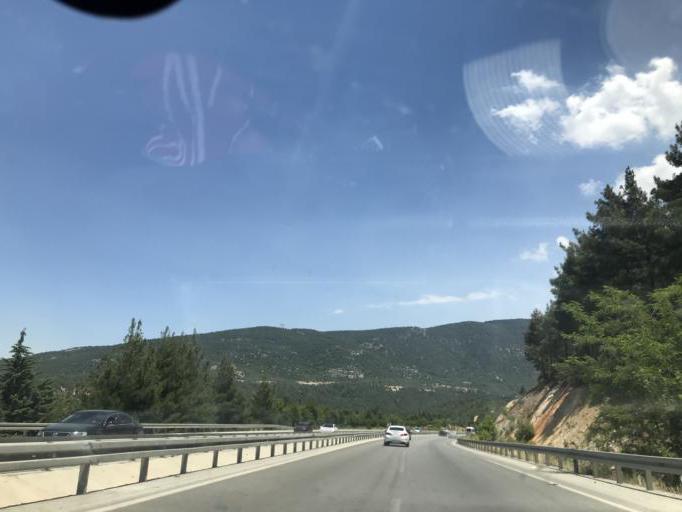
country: TR
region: Denizli
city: Honaz
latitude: 37.7303
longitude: 29.1889
